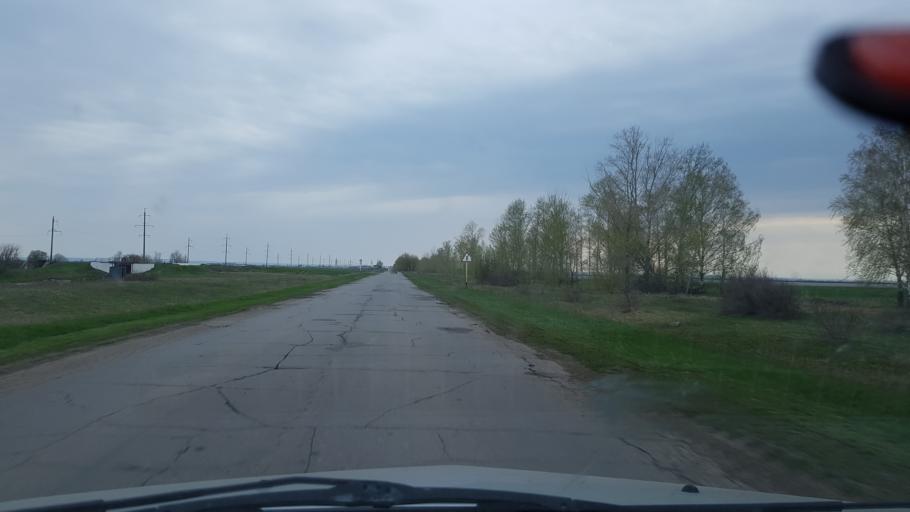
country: RU
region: Samara
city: Khryashchevka
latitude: 53.6692
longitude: 49.1271
